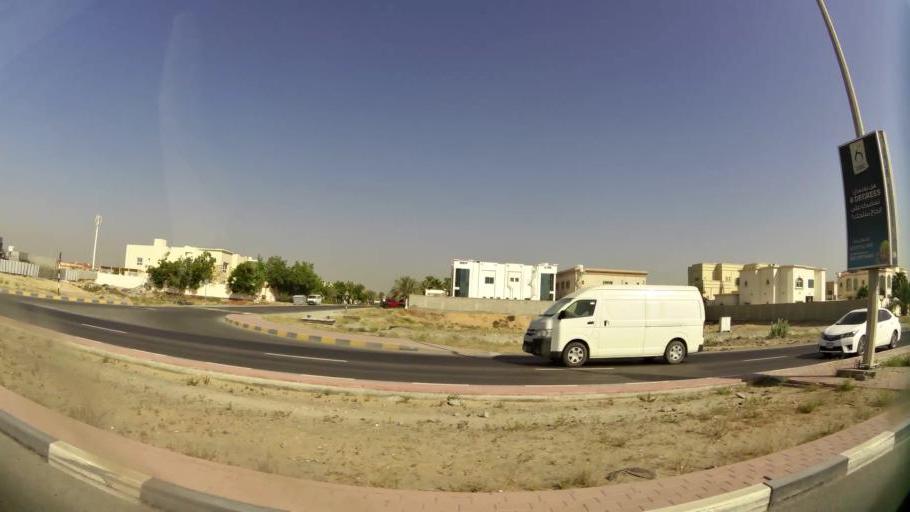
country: AE
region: Ajman
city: Ajman
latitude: 25.4160
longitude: 55.5121
